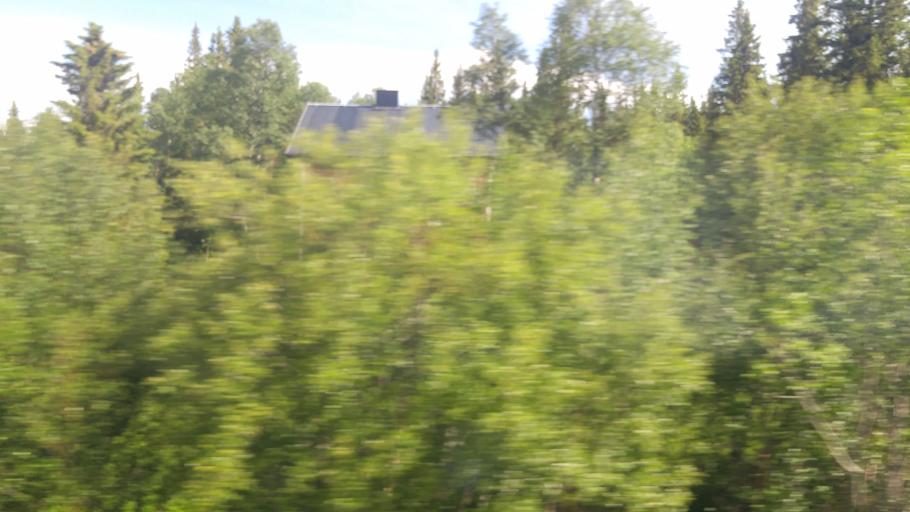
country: NO
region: Nord-Trondelag
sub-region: Meraker
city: Meraker
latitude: 63.2870
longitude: 12.3551
